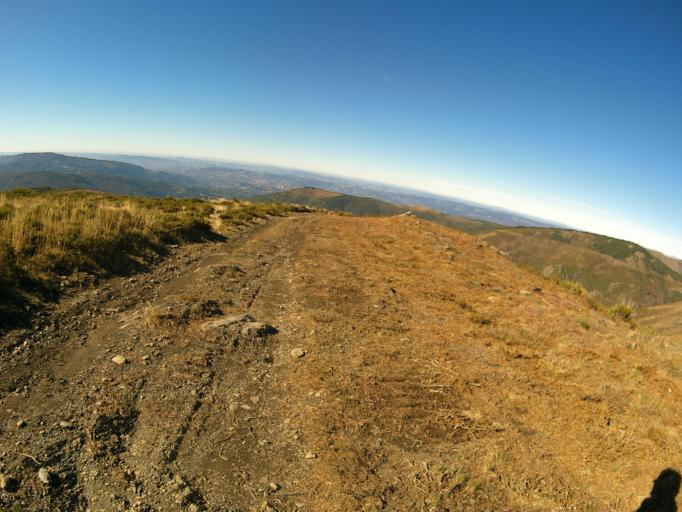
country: PT
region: Vila Real
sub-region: Mesao Frio
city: Mesao Frio
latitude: 41.2542
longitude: -7.9056
